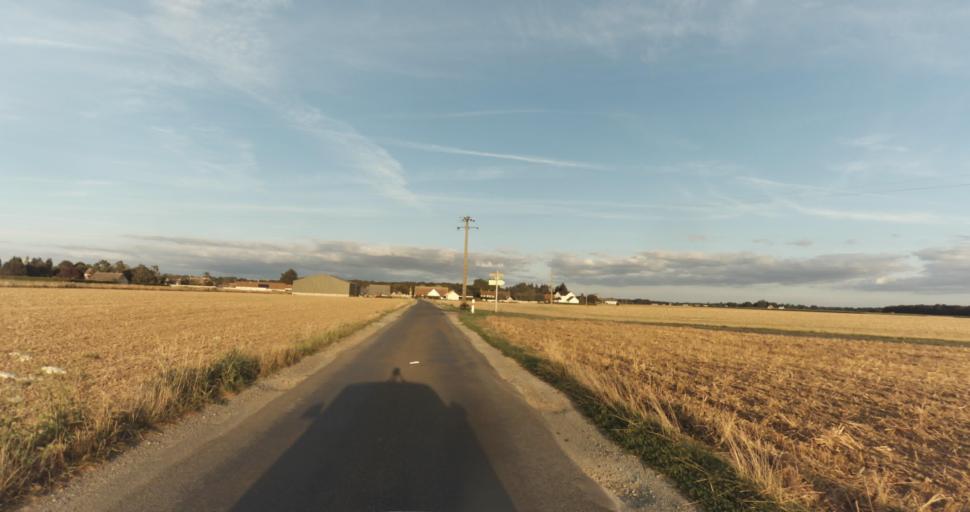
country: FR
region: Haute-Normandie
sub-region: Departement de l'Eure
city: Marcilly-sur-Eure
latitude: 48.8483
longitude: 1.2687
